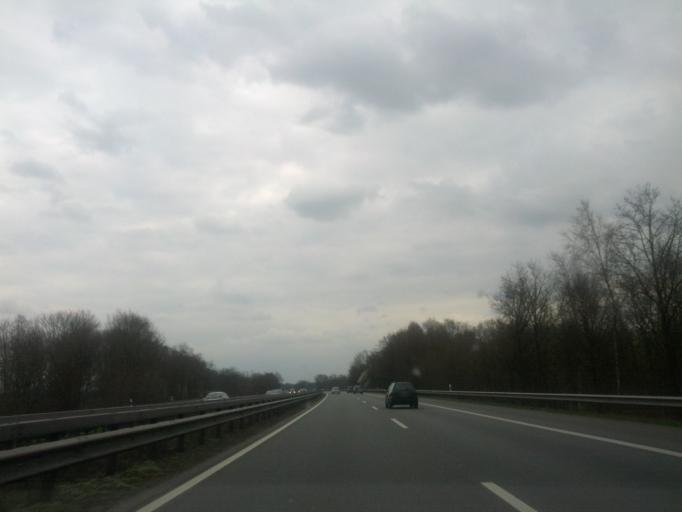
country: DE
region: Lower Saxony
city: Hatten
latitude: 53.0731
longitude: 8.3264
